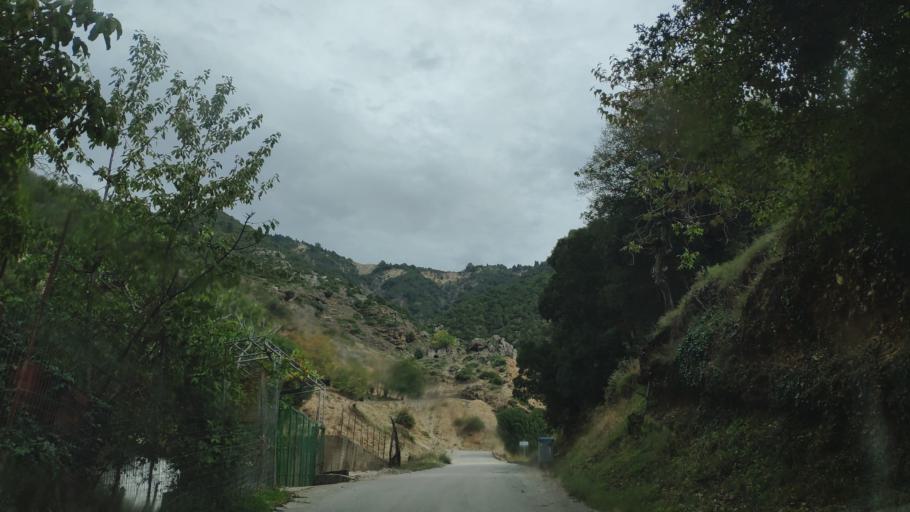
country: GR
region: Epirus
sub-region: Nomos Thesprotias
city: Paramythia
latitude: 39.4336
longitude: 20.6298
